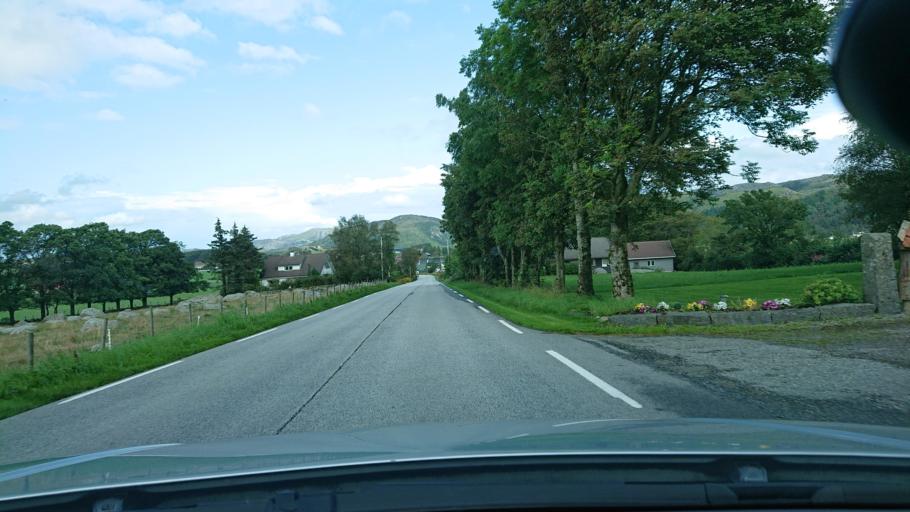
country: NO
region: Rogaland
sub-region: Gjesdal
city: Algard
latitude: 58.6946
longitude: 5.7769
